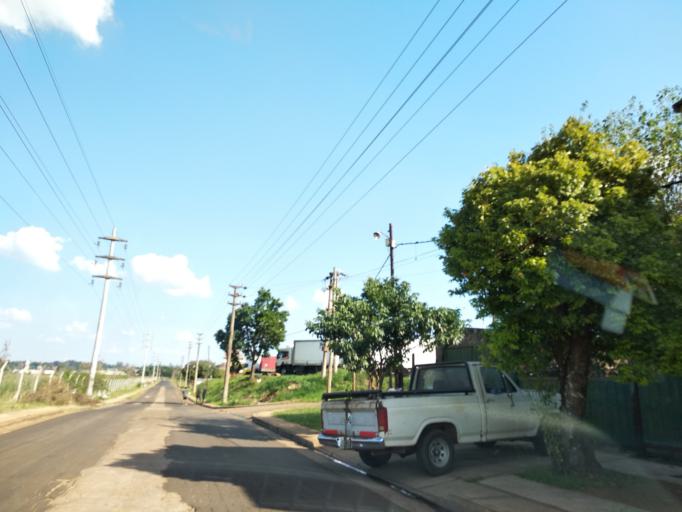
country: AR
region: Misiones
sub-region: Departamento de Capital
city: Posadas
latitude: -27.4083
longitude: -55.9011
